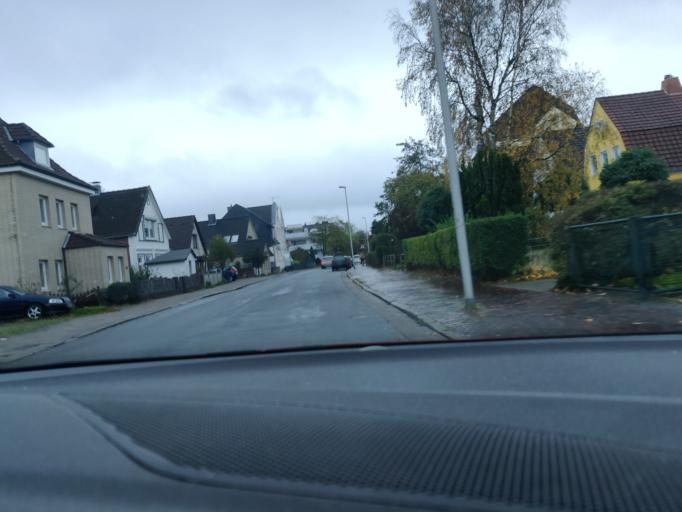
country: DE
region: Lower Saxony
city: Cuxhaven
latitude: 53.8800
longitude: 8.6808
